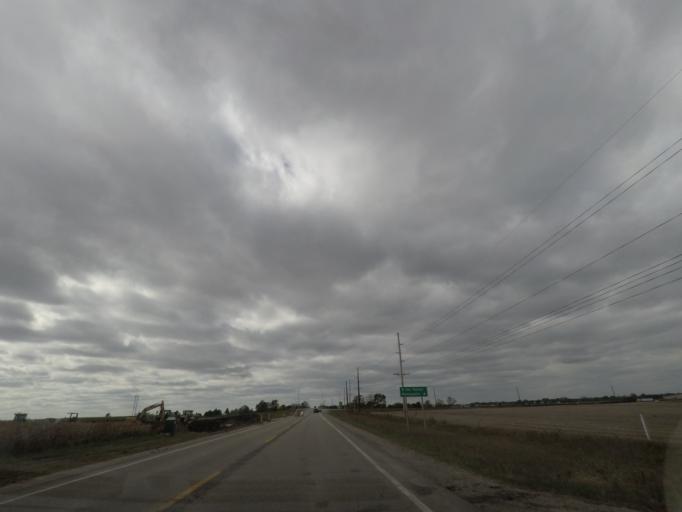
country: US
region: Iowa
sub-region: Story County
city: Huxley
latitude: 41.8778
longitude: -93.5657
